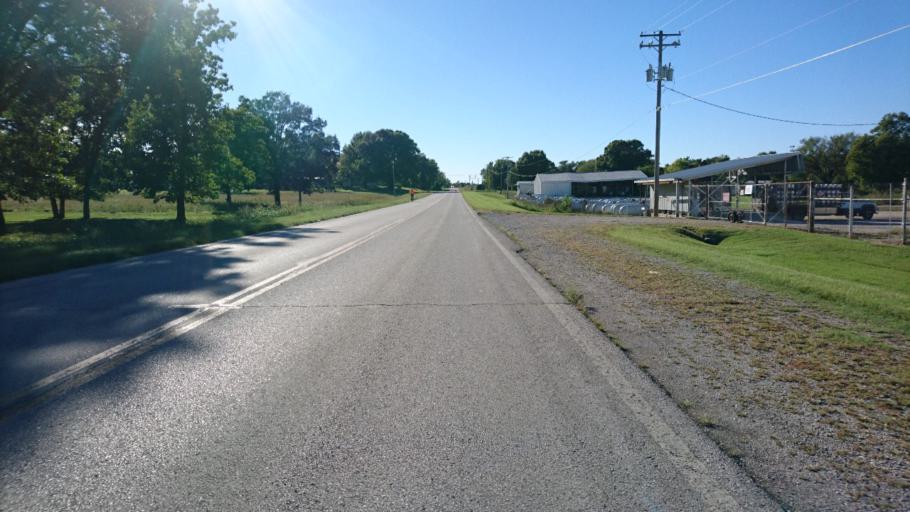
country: US
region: Missouri
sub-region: Jasper County
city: Carthage
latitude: 37.1732
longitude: -94.3548
